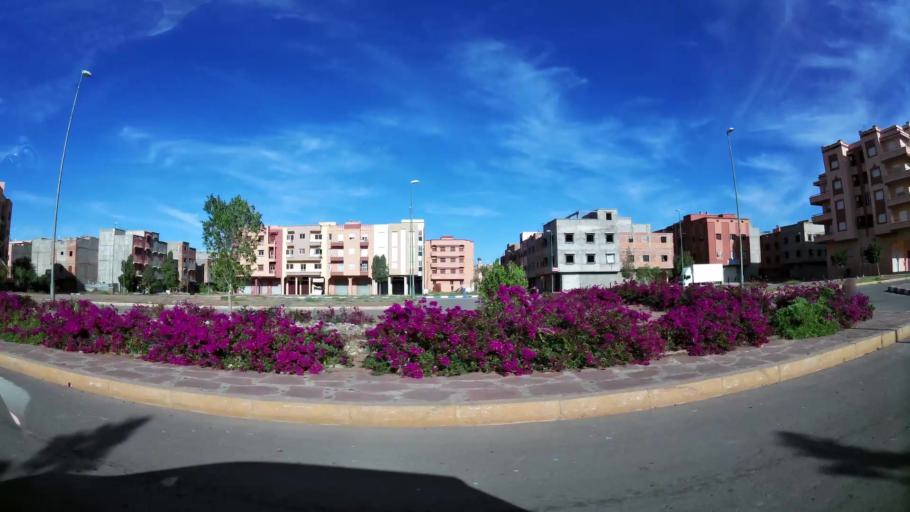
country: MA
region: Marrakech-Tensift-Al Haouz
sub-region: Marrakech
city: Marrakesh
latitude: 31.6877
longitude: -8.0688
